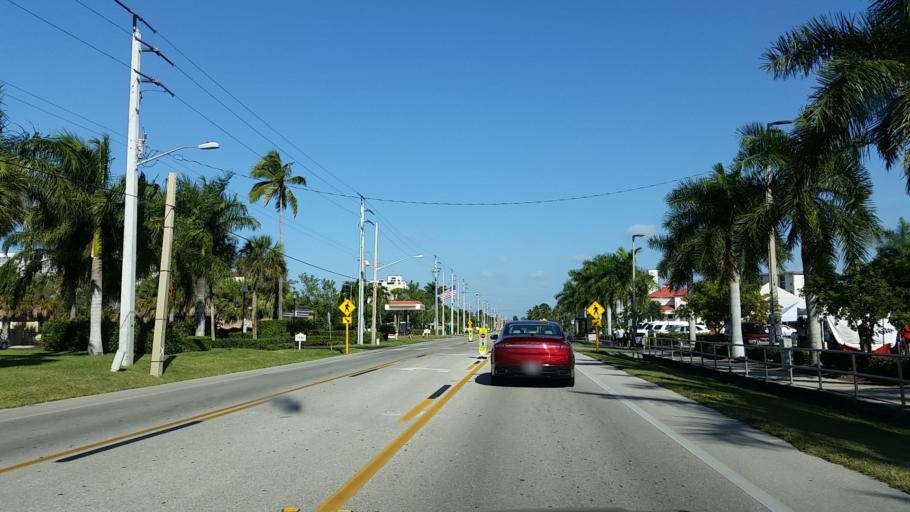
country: US
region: Florida
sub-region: Lee County
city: Fort Myers Beach
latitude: 26.4138
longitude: -81.9002
